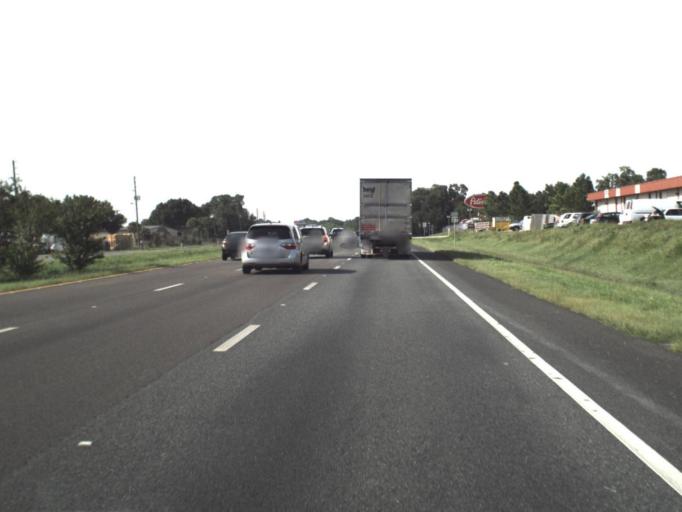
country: US
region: Florida
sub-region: Polk County
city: Lake Hamilton
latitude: 28.0557
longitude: -81.6352
